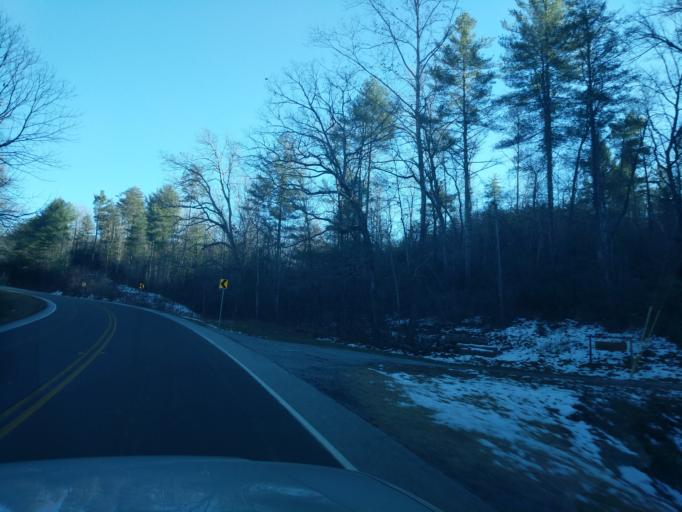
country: US
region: Georgia
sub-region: Rabun County
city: Clayton
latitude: 34.8364
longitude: -83.3316
